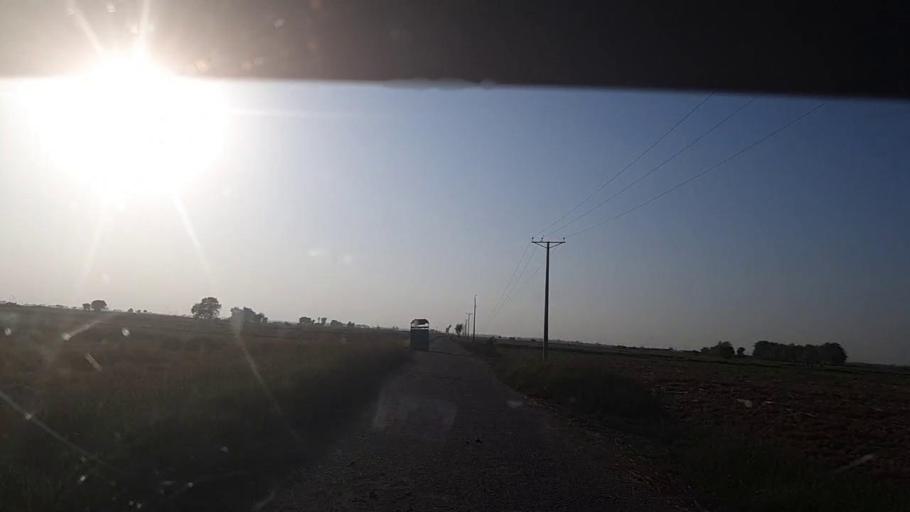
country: PK
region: Sindh
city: Ratodero
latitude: 27.8521
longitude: 68.2213
